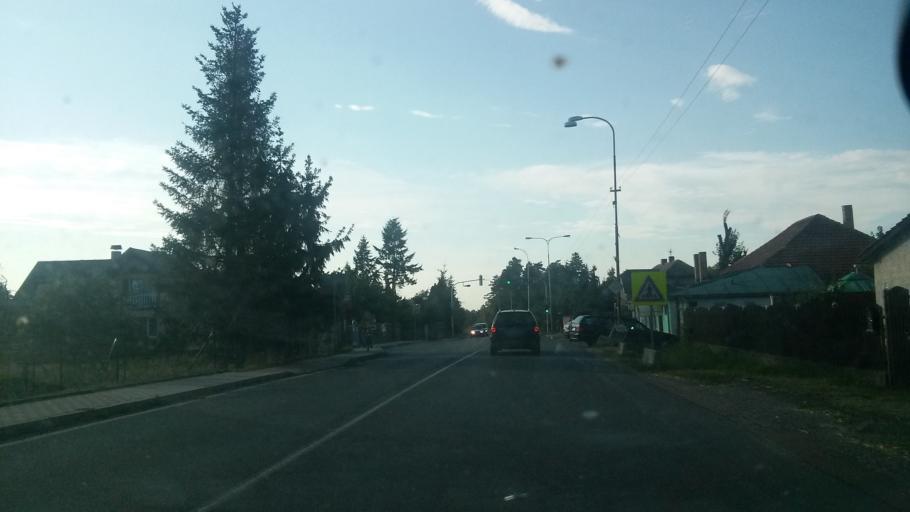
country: CZ
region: Central Bohemia
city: Jesenice
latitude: 49.9517
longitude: 14.5383
